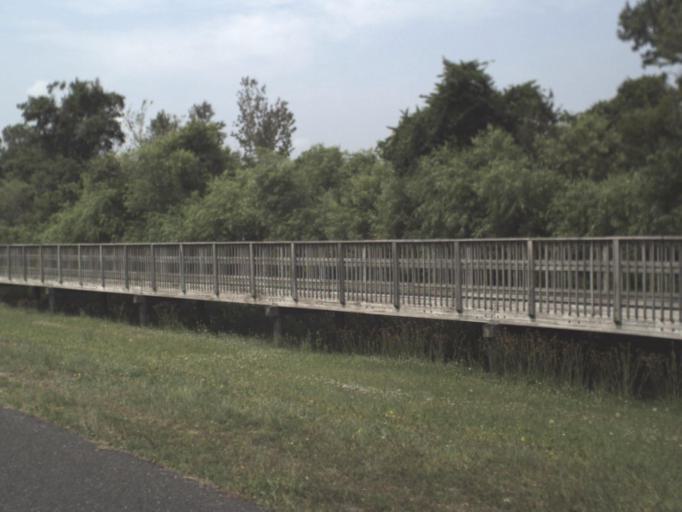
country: US
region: Florida
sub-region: Clay County
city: Orange Park
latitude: 30.1272
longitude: -81.7039
